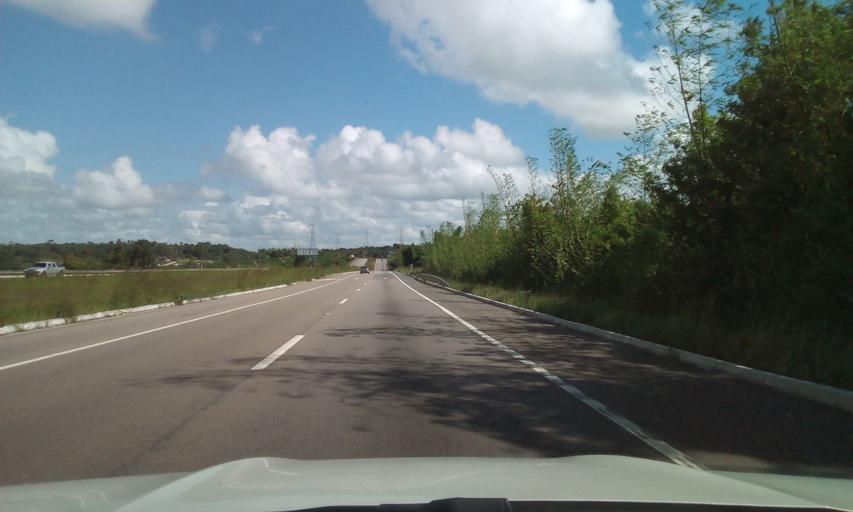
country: BR
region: Paraiba
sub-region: Conde
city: Conde
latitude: -7.3071
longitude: -34.9429
